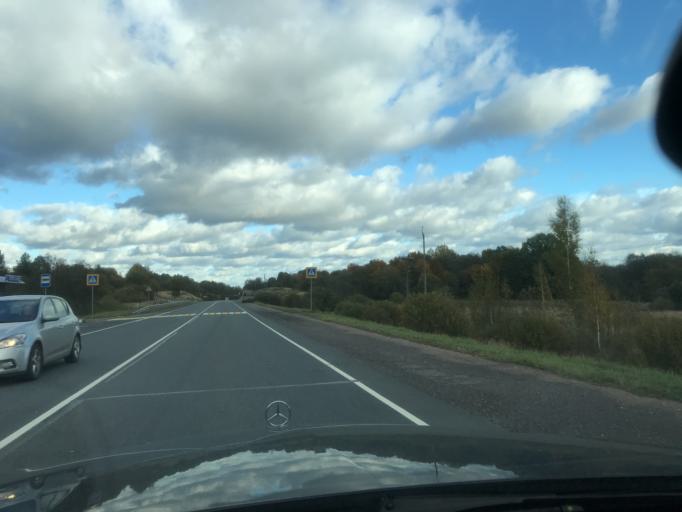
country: RU
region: Pskov
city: Novosokol'niki
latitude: 56.3486
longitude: 29.9094
